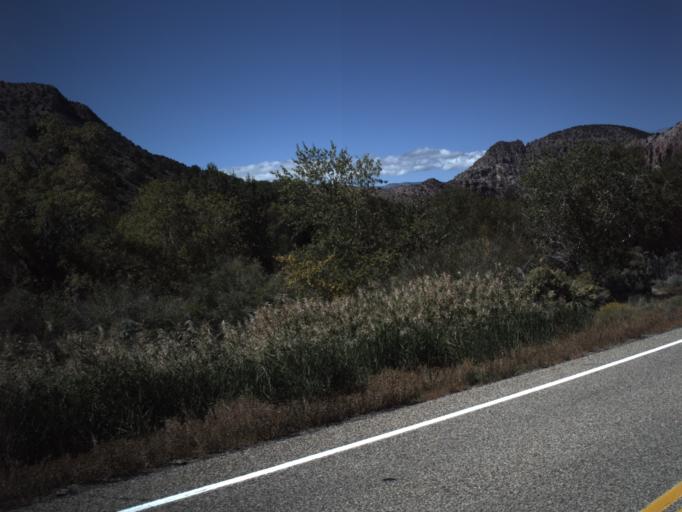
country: US
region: Utah
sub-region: Piute County
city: Junction
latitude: 38.1904
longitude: -112.1023
